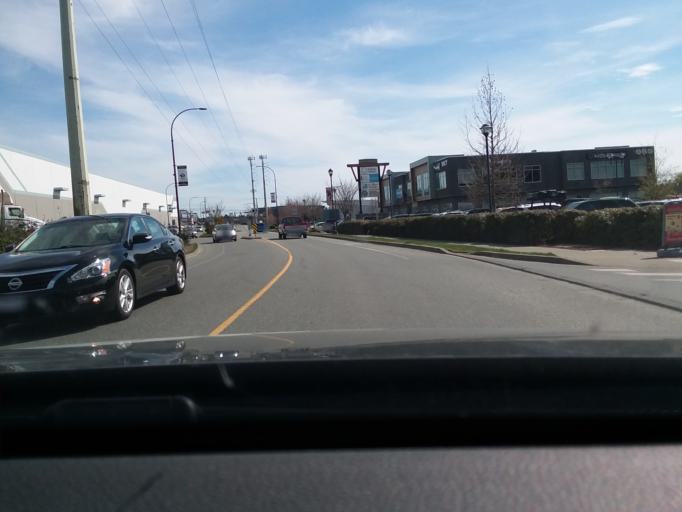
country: CA
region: British Columbia
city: Langford
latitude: 48.4429
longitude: -123.5145
